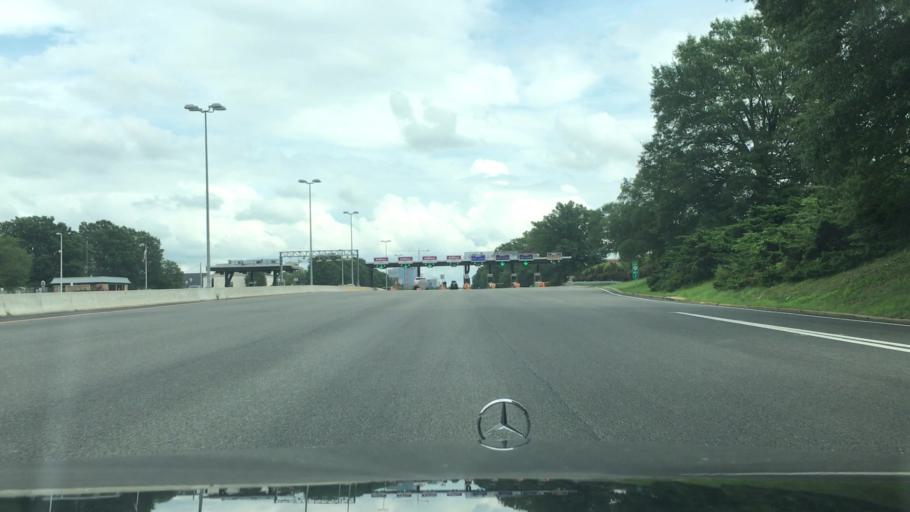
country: US
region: Virginia
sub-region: City of Richmond
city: Richmond
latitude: 37.5456
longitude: -77.4638
